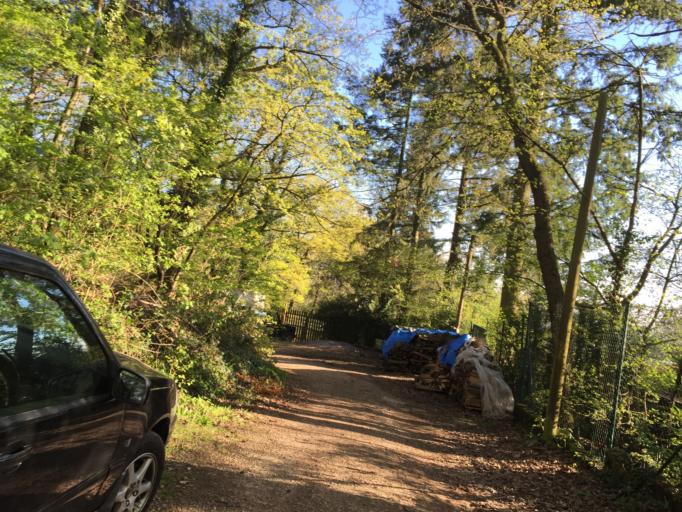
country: DE
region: Baden-Wuerttemberg
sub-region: Karlsruhe Region
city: Weinheim
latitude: 49.5111
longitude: 8.6737
